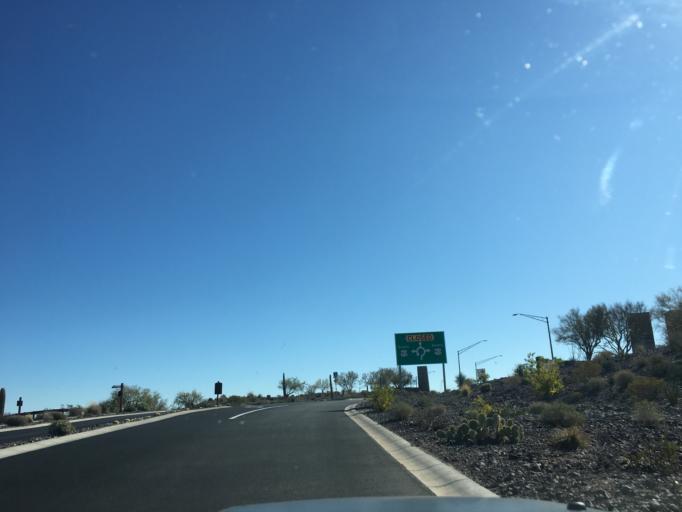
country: US
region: Arizona
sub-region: Maricopa County
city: Wickenburg
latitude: 34.0182
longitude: -112.7981
